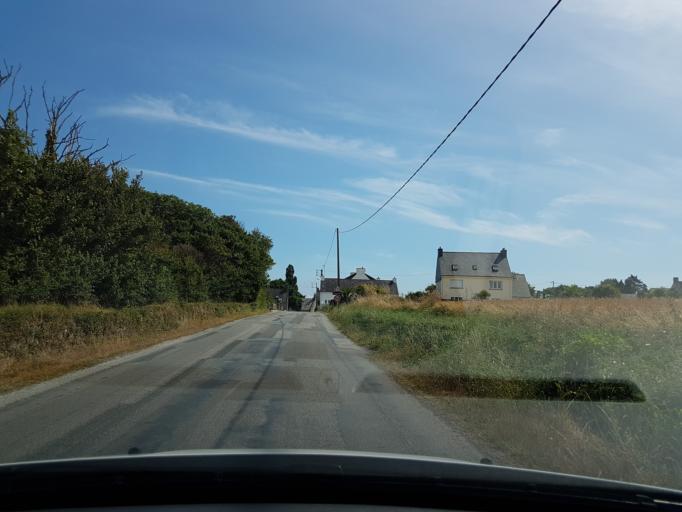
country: FR
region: Brittany
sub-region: Departement du Morbihan
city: Etel
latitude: 47.6722
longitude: -3.2210
